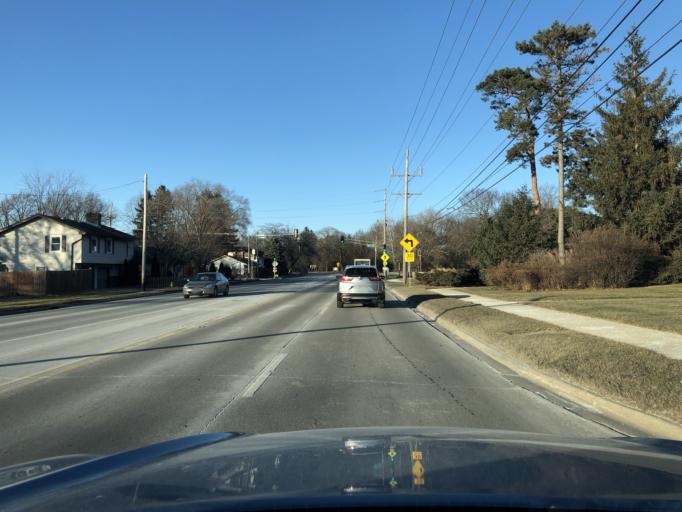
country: US
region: Illinois
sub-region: Cook County
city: Barrington
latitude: 42.1588
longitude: -88.1283
